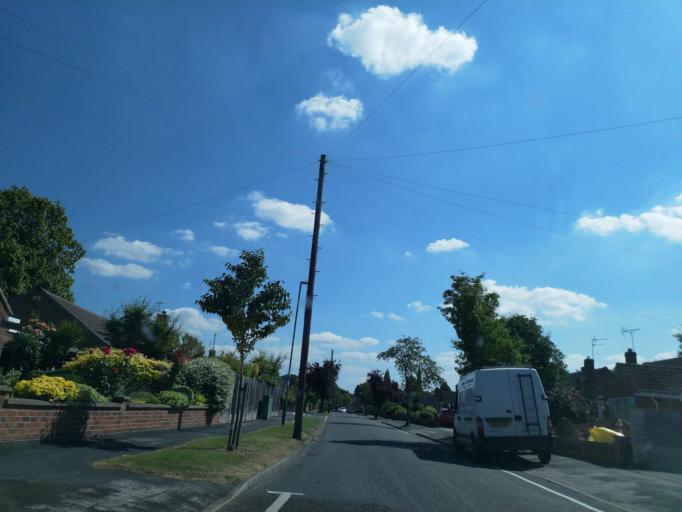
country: GB
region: England
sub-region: Warwickshire
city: Kenilworth
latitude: 52.3410
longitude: -1.5718
